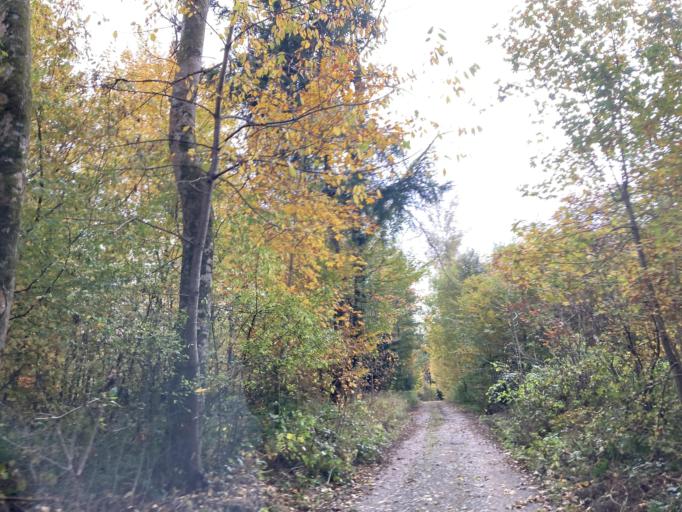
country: DE
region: Baden-Wuerttemberg
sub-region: Tuebingen Region
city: Ofterdingen
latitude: 48.4351
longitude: 9.0058
